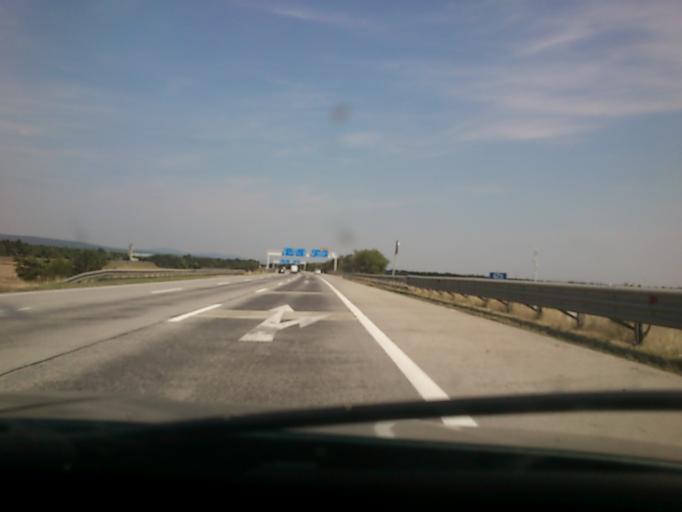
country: AT
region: Lower Austria
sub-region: Wiener Neustadt Stadt
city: Wiener Neustadt
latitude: 47.7773
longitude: 16.2063
